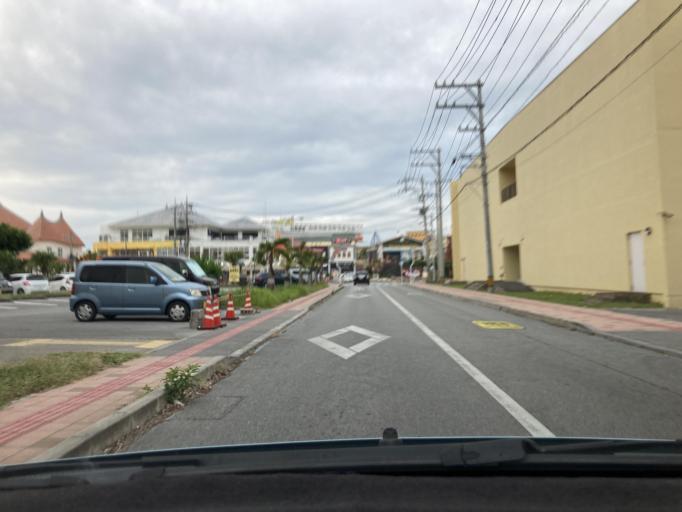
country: JP
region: Okinawa
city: Chatan
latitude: 26.3148
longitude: 127.7565
